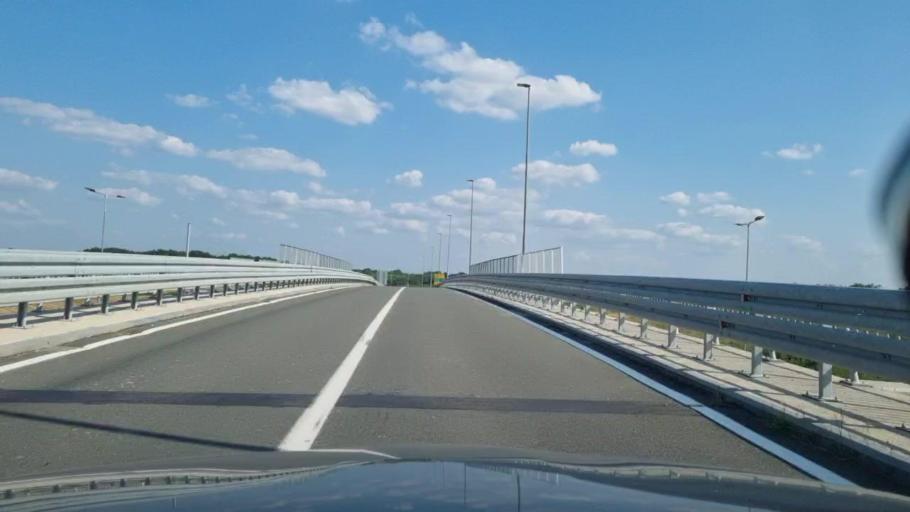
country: BA
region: Federation of Bosnia and Herzegovina
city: Odzak
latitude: 45.1000
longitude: 18.2988
